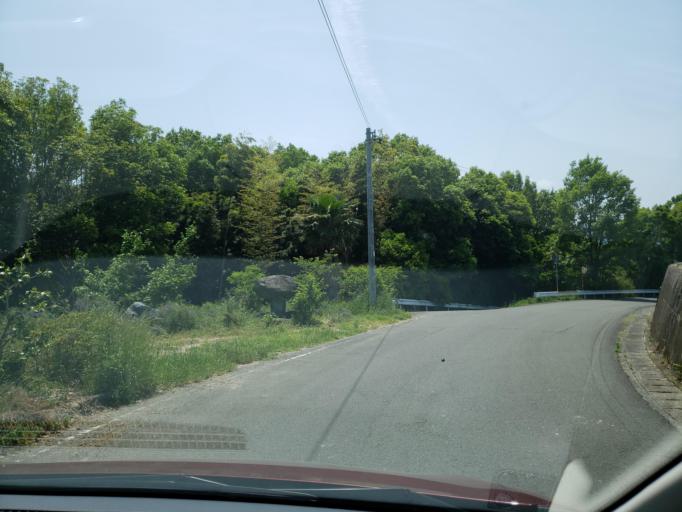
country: JP
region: Tokushima
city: Wakimachi
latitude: 34.0842
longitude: 134.2082
